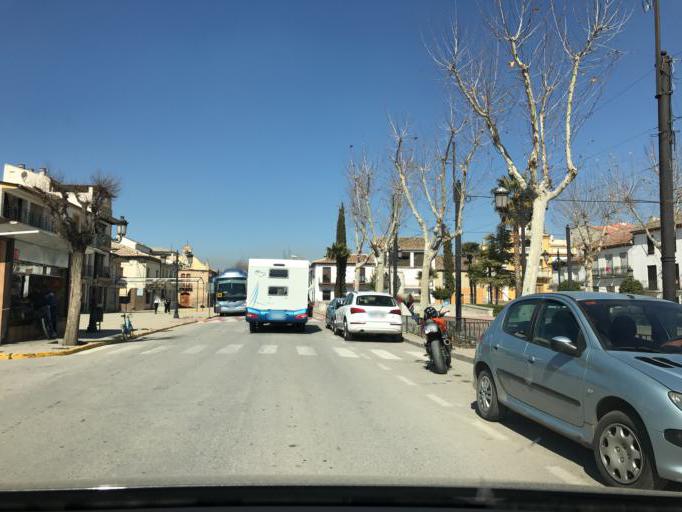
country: ES
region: Andalusia
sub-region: Provincia de Granada
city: Fuente Vaqueros
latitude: 37.2200
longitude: -3.7839
